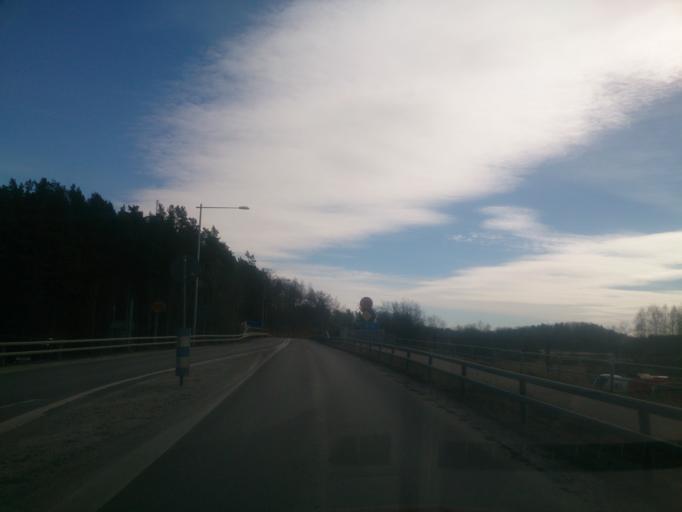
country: SE
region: OEstergoetland
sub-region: Norrkopings Kommun
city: Kimstad
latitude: 58.5455
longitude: 15.9705
